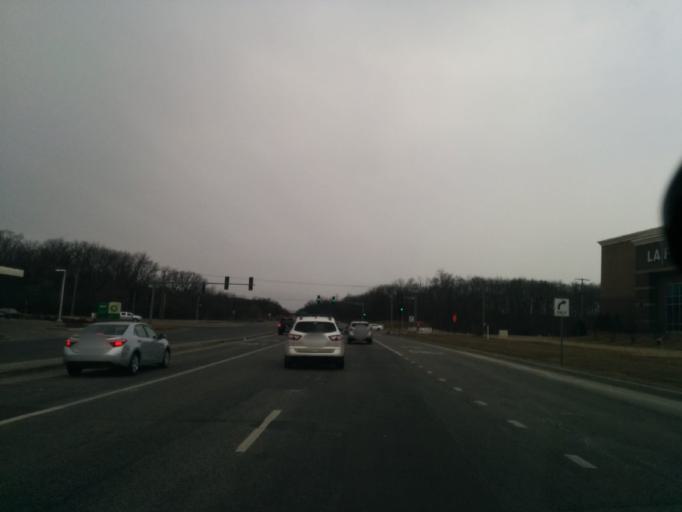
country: US
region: Illinois
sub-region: Cook County
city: Northbrook
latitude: 42.1093
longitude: -87.8751
